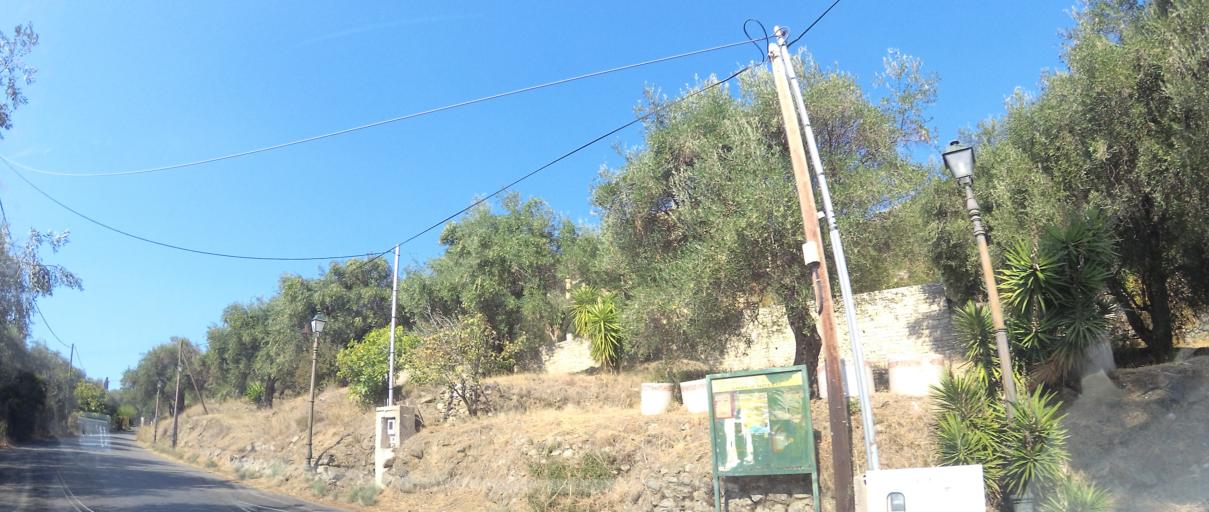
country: GR
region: Ionian Islands
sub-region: Nomos Kerkyras
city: Kontokali
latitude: 39.7210
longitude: 19.8472
